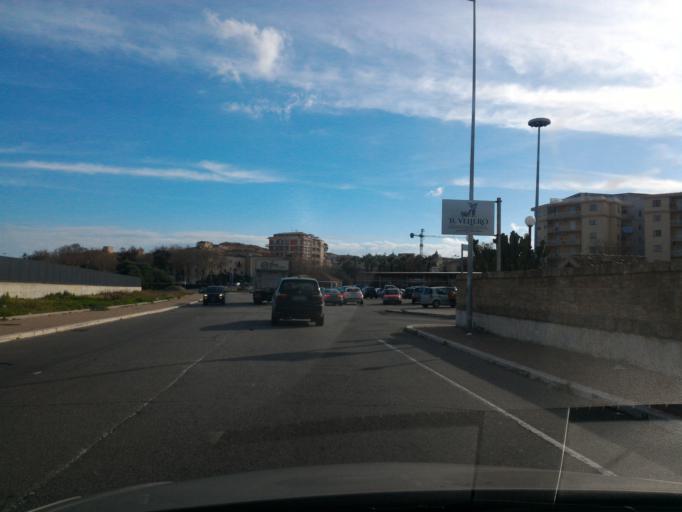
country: IT
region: Calabria
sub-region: Provincia di Crotone
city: Crotone
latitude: 39.0842
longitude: 17.1247
